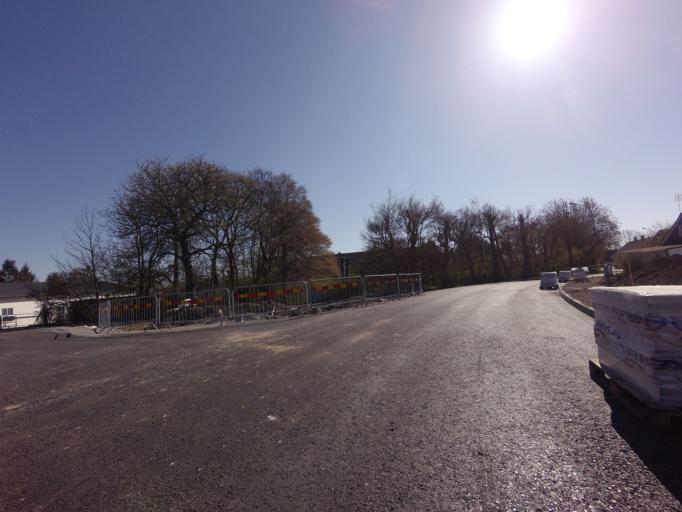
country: SE
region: Skane
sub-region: Malmo
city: Oxie
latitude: 55.4703
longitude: 13.1347
